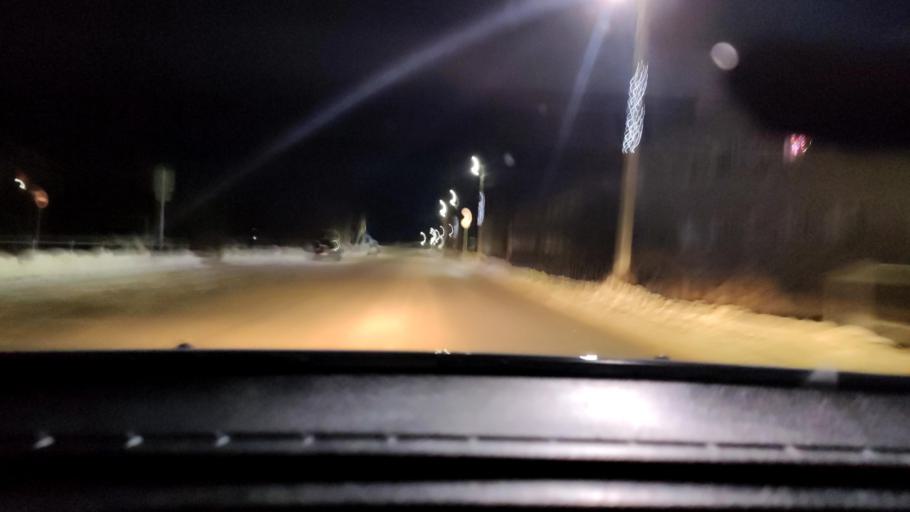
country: RU
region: Voronezj
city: Ramon'
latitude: 51.9147
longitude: 39.3327
